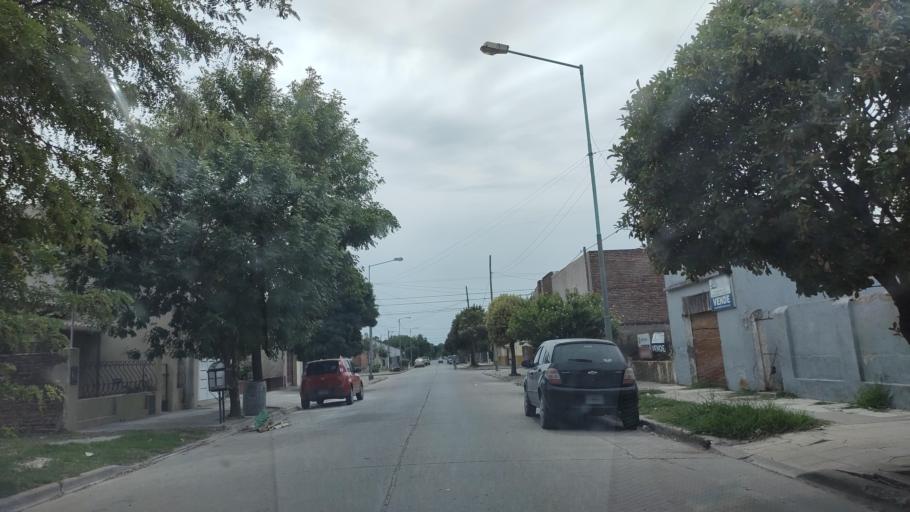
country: AR
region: Buenos Aires
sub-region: Partido de Loberia
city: Loberia
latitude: -38.1651
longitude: -58.7776
